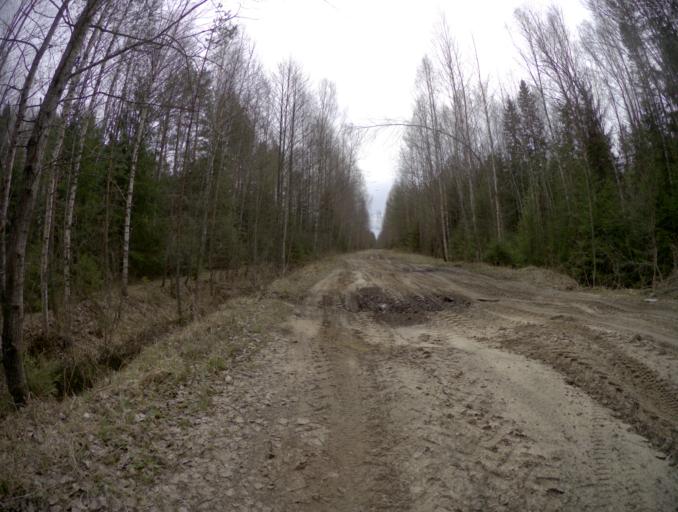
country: RU
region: Vladimir
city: Raduzhnyy
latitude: 55.9330
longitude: 40.2444
